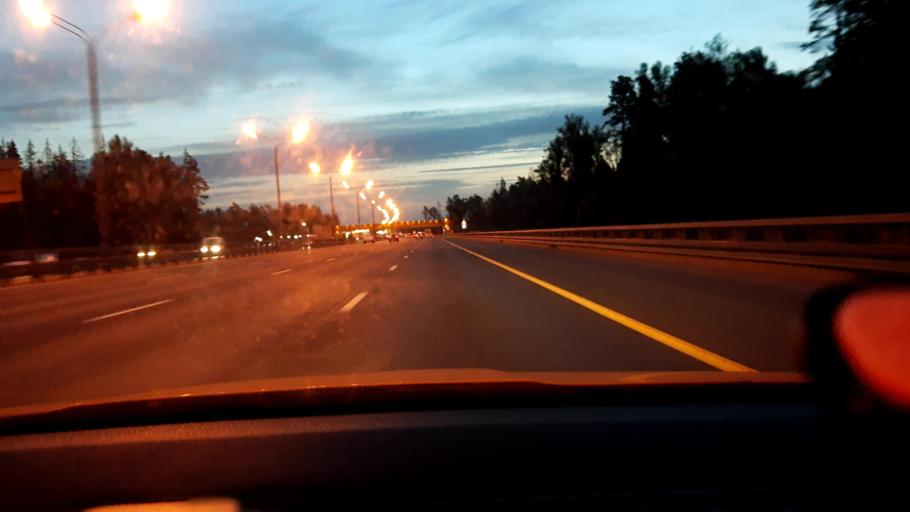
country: RU
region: Moskovskaya
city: Krasnoznamensk
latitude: 55.6097
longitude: 37.0619
